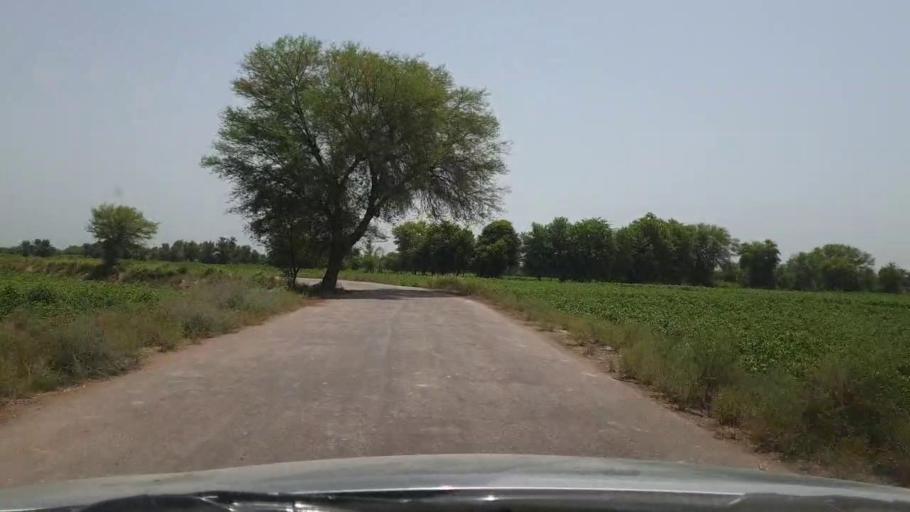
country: PK
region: Sindh
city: Pano Aqil
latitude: 27.8789
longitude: 69.1470
